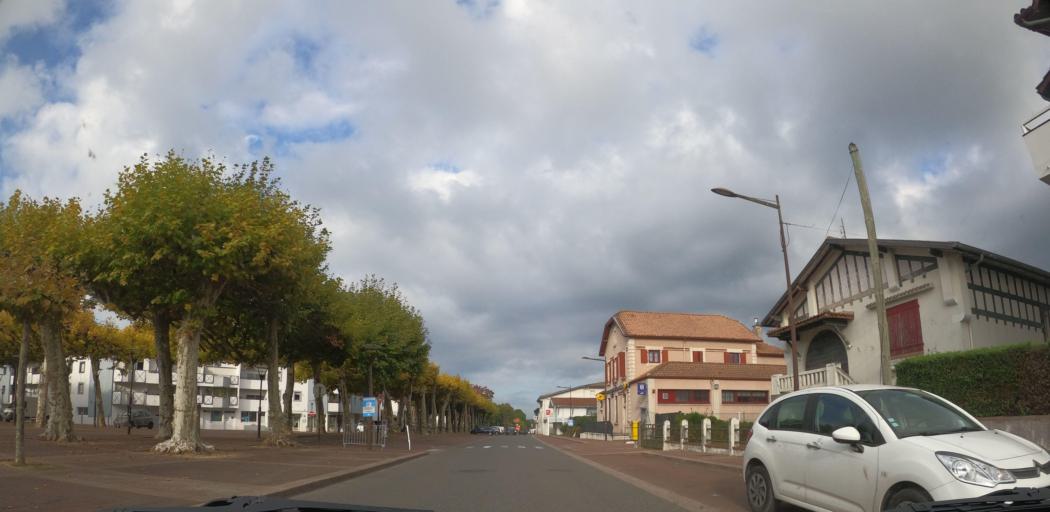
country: FR
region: Aquitaine
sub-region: Departement des Landes
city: Soustons
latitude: 43.7535
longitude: -1.3263
